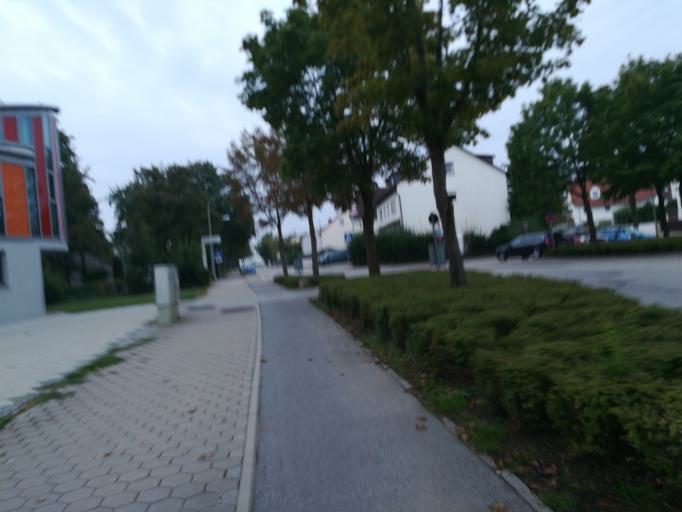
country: DE
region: Bavaria
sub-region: Upper Bavaria
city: Karlsfeld
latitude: 48.2272
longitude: 11.4754
